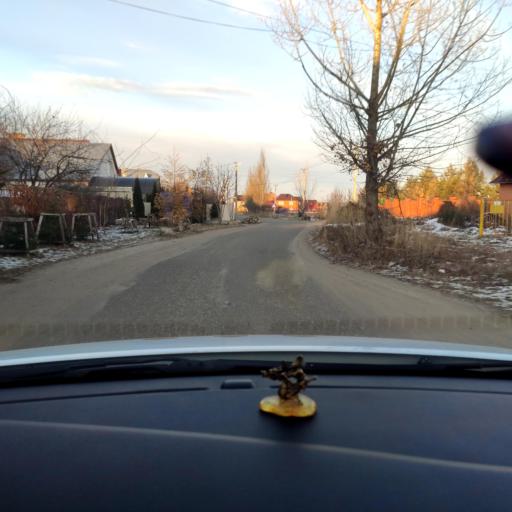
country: RU
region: Tatarstan
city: Stolbishchi
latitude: 55.6081
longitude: 49.1480
